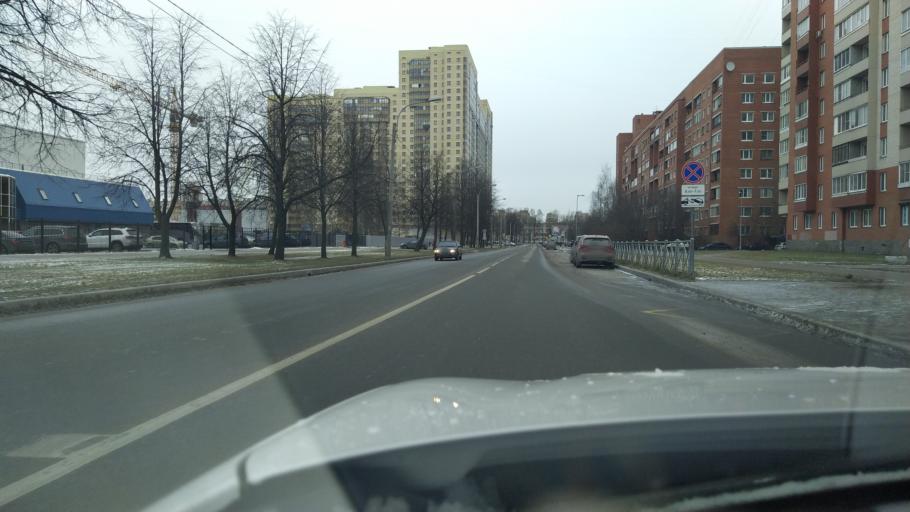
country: RU
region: Leningrad
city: Akademicheskoe
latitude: 60.0077
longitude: 30.4026
